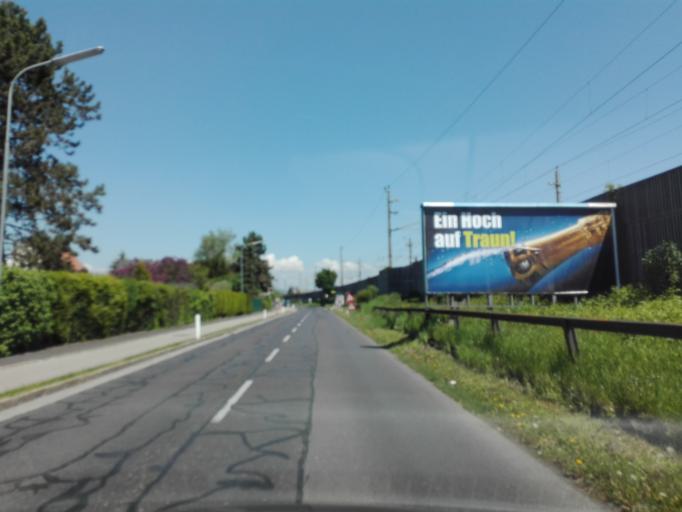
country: AT
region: Upper Austria
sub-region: Politischer Bezirk Linz-Land
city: Traun
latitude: 48.2296
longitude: 14.2573
